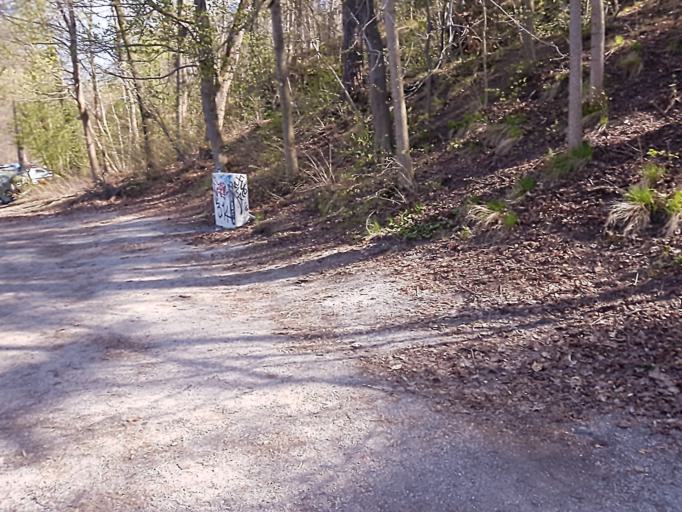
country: SE
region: Stockholm
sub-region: Stockholms Kommun
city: Arsta
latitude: 59.3016
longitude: 18.0735
